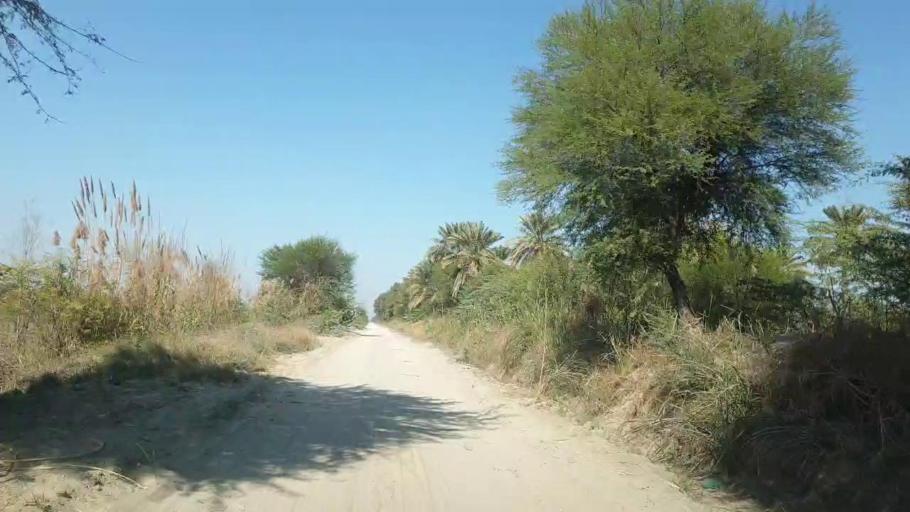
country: PK
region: Sindh
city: Mirpur Khas
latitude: 25.6506
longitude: 69.0274
